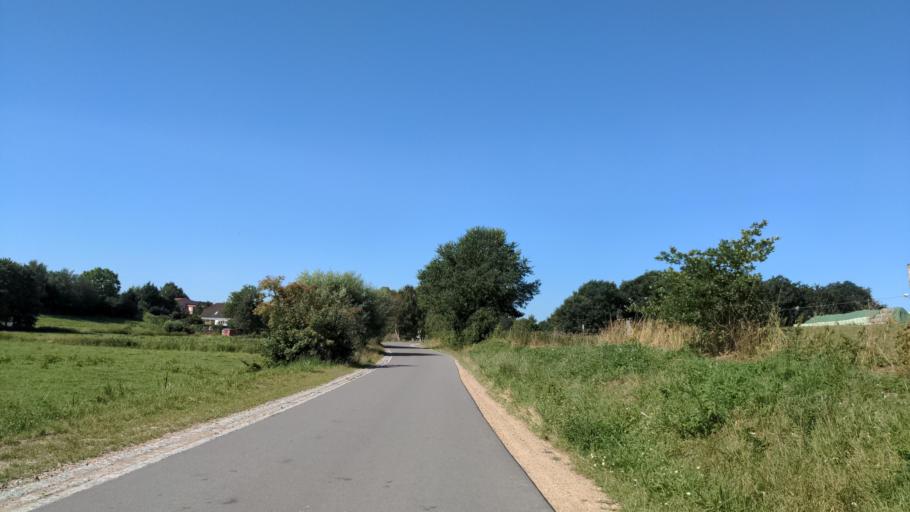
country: DE
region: Mecklenburg-Vorpommern
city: Selmsdorf
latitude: 53.8366
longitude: 10.8728
